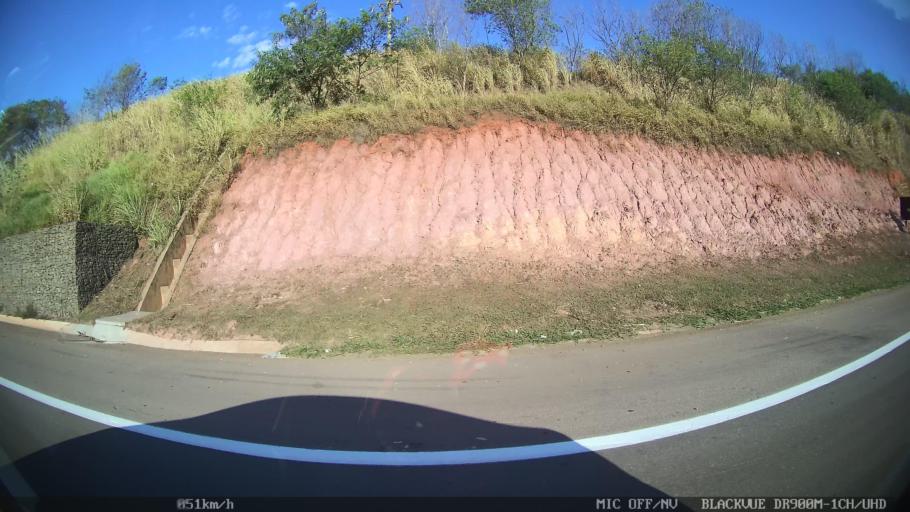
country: BR
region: Sao Paulo
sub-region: Piracicaba
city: Piracicaba
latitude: -22.6648
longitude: -47.6170
